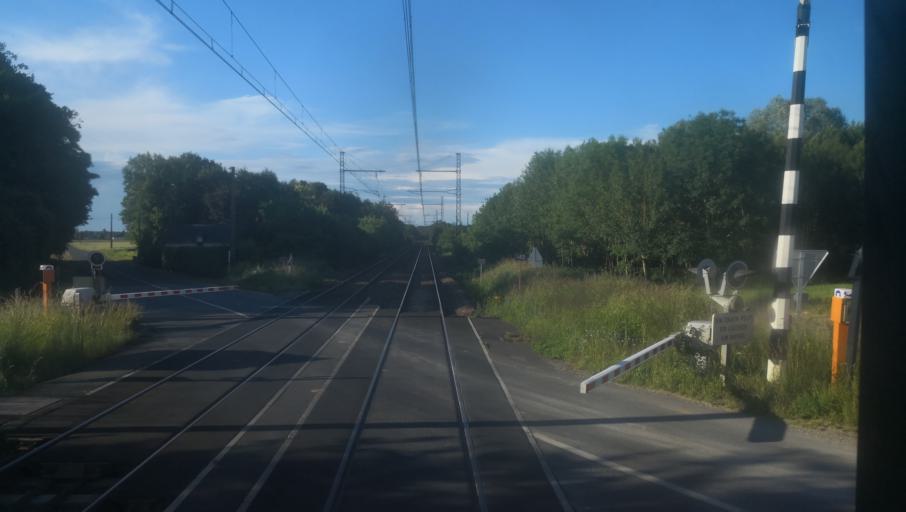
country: FR
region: Centre
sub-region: Departement du Cher
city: Mereau
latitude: 47.1495
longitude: 2.0517
